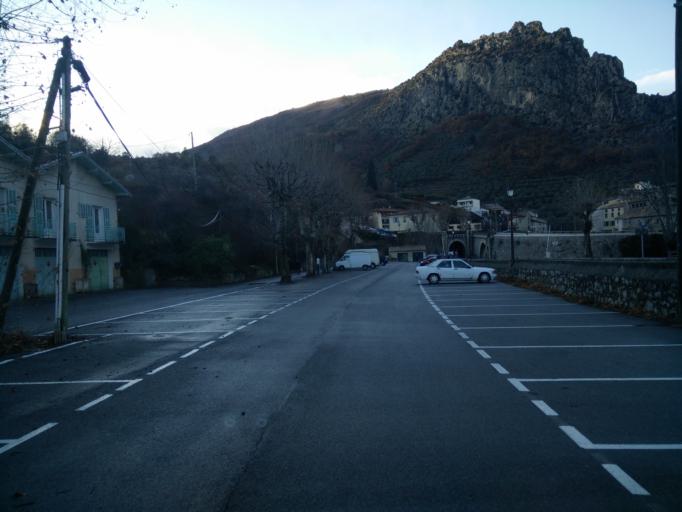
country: FR
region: Provence-Alpes-Cote d'Azur
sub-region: Departement des Alpes-Maritimes
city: Puget-Theniers
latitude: 43.9489
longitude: 6.8132
